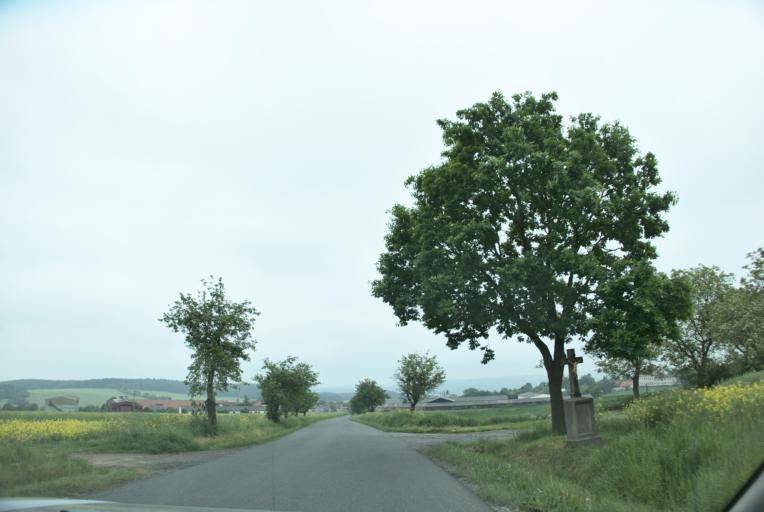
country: CZ
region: Plzensky
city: Zihle
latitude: 50.0120
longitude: 13.4118
